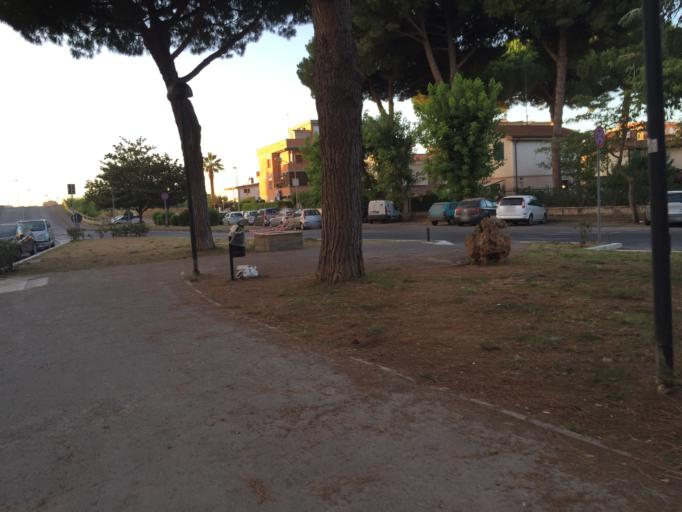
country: IT
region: Latium
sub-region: Citta metropolitana di Roma Capitale
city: Ladispoli
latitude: 41.9555
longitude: 12.0674
